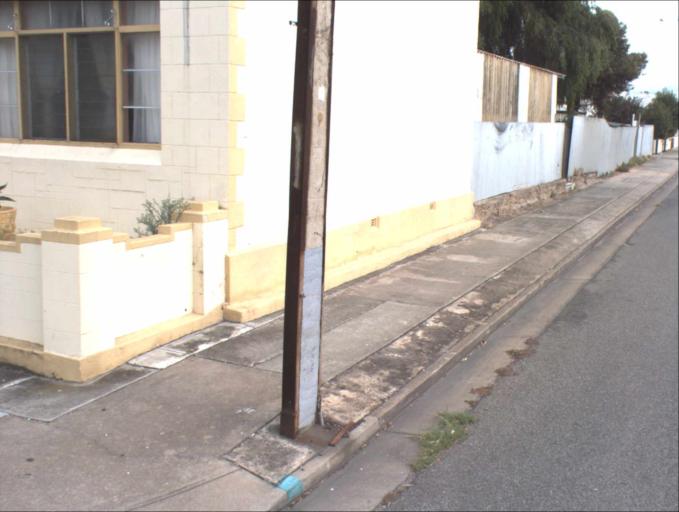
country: AU
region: South Australia
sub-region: Port Adelaide Enfield
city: Birkenhead
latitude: -34.8295
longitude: 138.4973
